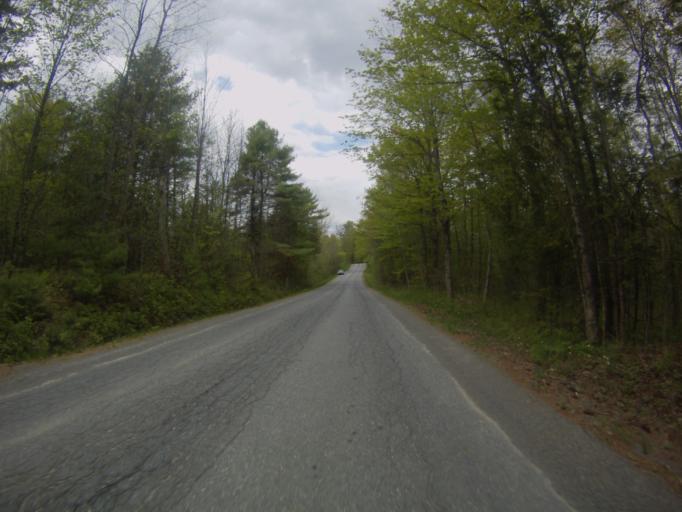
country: US
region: New York
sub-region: Essex County
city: Ticonderoga
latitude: 43.9289
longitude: -73.5055
